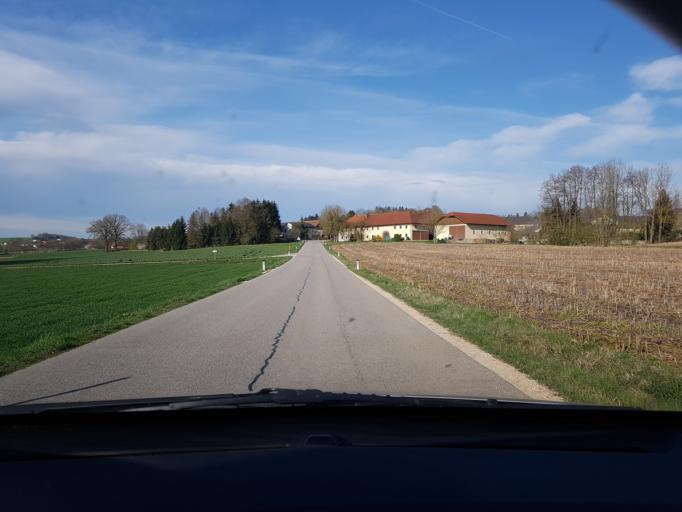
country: AT
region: Upper Austria
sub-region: Politischer Bezirk Linz-Land
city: Sankt Florian
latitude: 48.1612
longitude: 14.4028
